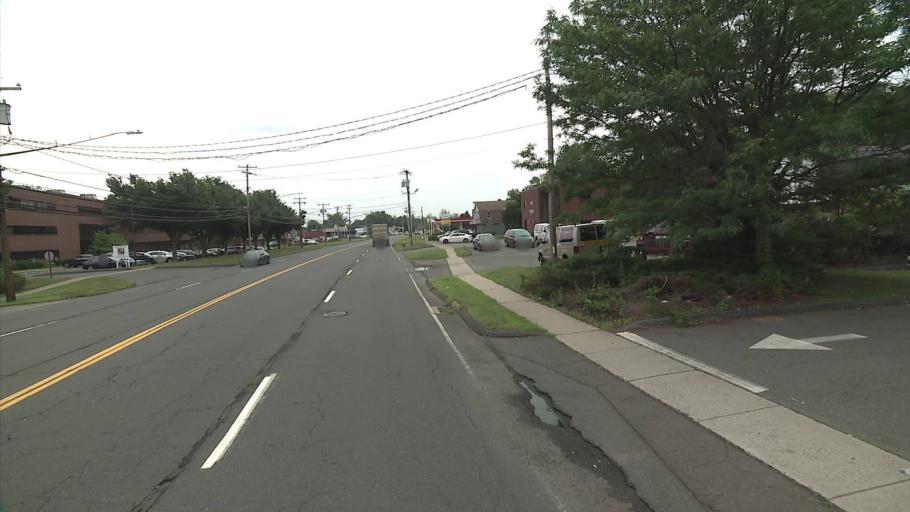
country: US
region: Connecticut
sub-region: Hartford County
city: Wethersfield
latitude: 41.6717
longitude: -72.6447
